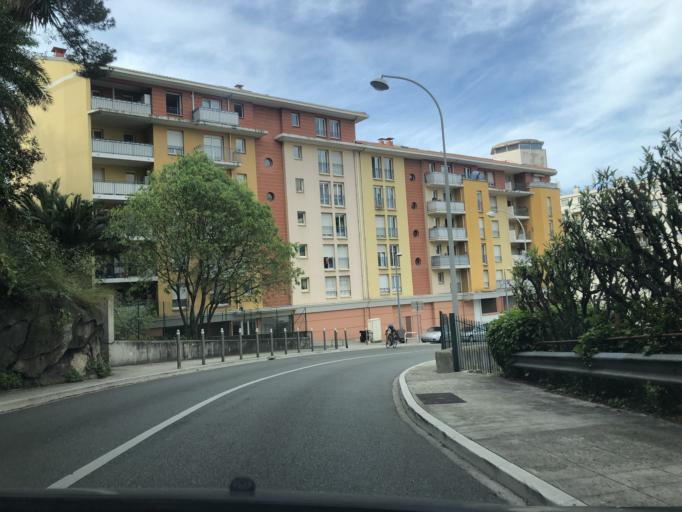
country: FR
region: Provence-Alpes-Cote d'Azur
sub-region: Departement des Alpes-Maritimes
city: Villefranche-sur-Mer
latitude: 43.7085
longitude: 7.2938
